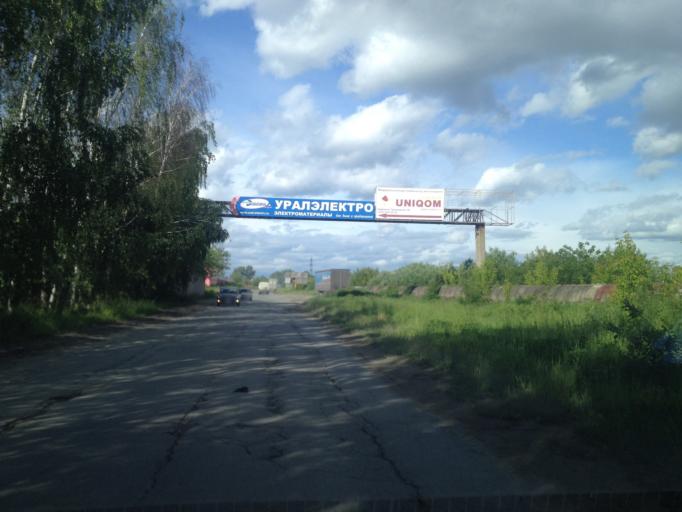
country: RU
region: Sverdlovsk
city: Yekaterinburg
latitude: 56.8755
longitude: 60.5436
